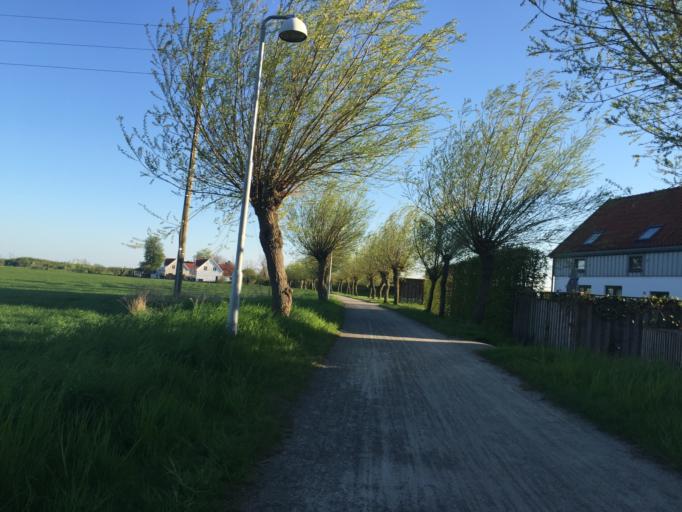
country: SE
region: Skane
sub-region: Malmo
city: Bunkeflostrand
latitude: 55.5536
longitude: 12.9667
